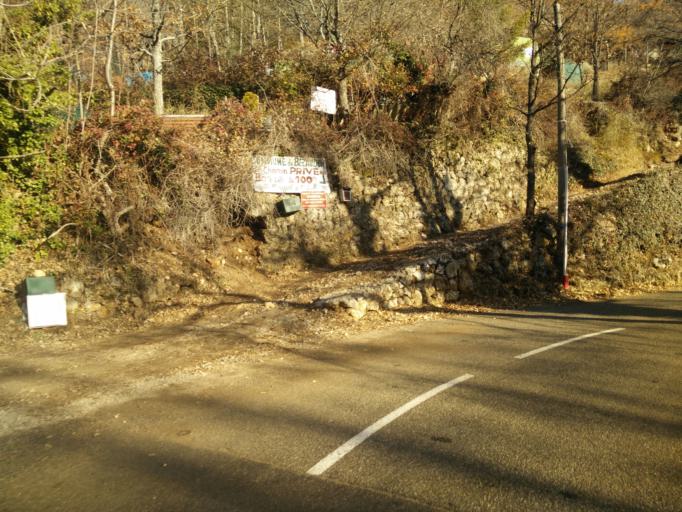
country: FR
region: Provence-Alpes-Cote d'Azur
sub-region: Departement des Alpes-Maritimes
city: Le Broc
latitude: 43.8120
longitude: 7.0929
